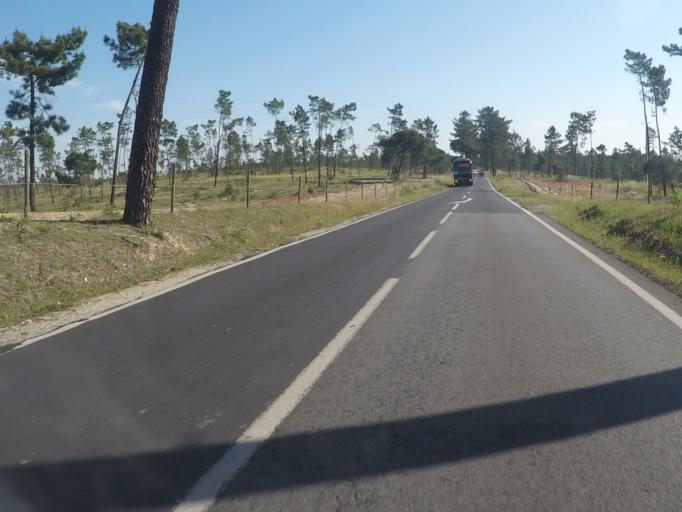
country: PT
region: Setubal
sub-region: Seixal
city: Arrentela
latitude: 38.5375
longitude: -9.1166
